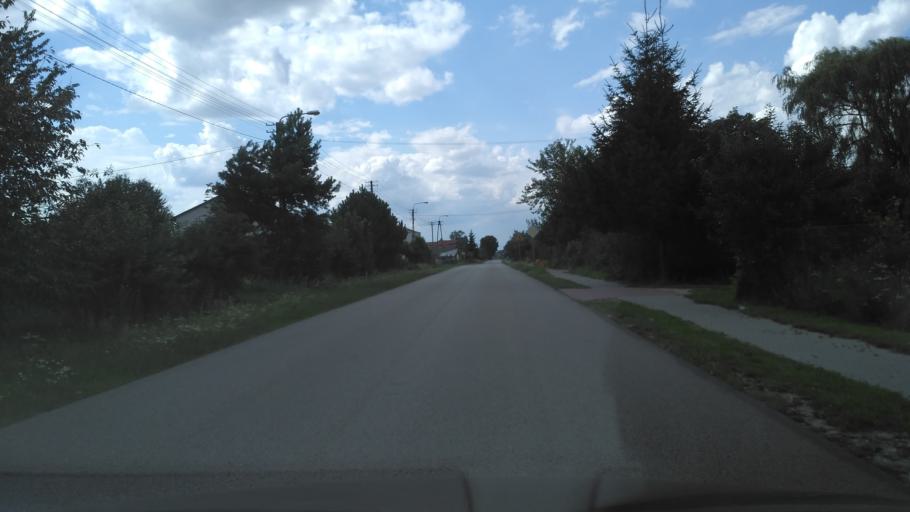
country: PL
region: Lublin Voivodeship
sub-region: Powiat swidnicki
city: Trawniki
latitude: 51.1735
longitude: 22.9748
